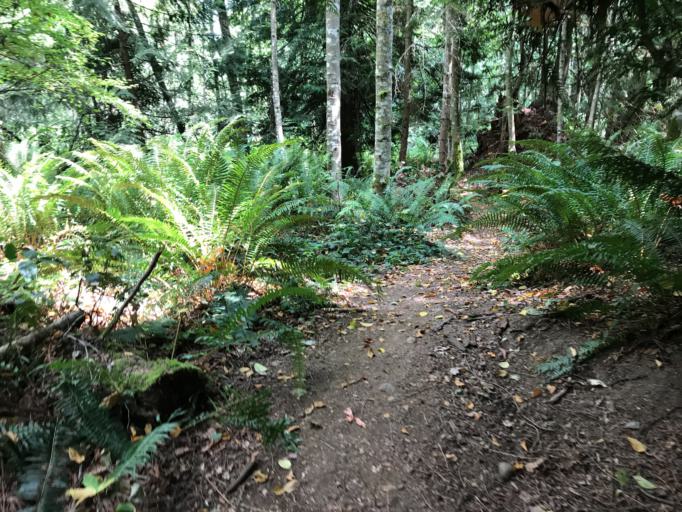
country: CA
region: British Columbia
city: North Cowichan
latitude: 48.9267
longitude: -123.7374
